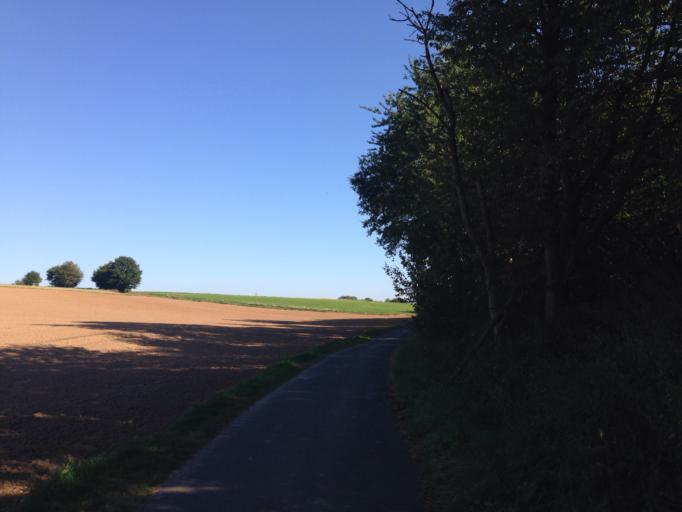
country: DE
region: Hesse
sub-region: Regierungsbezirk Giessen
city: Grunberg
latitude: 50.6196
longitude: 8.9468
